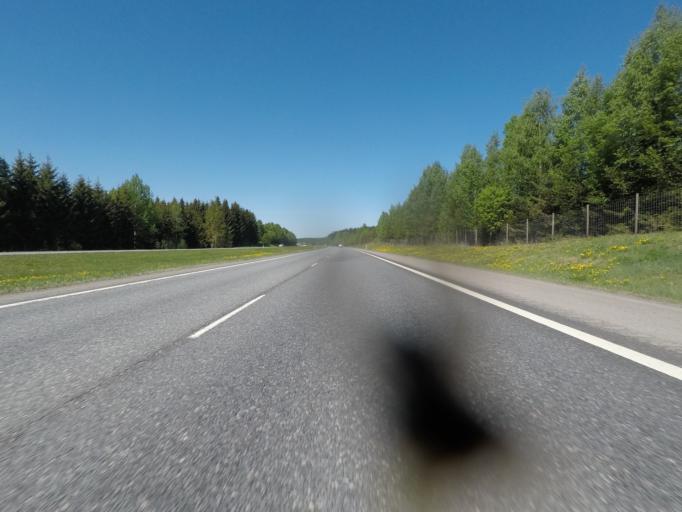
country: FI
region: Haeme
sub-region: Haemeenlinna
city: Tervakoski
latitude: 60.8366
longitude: 24.6478
